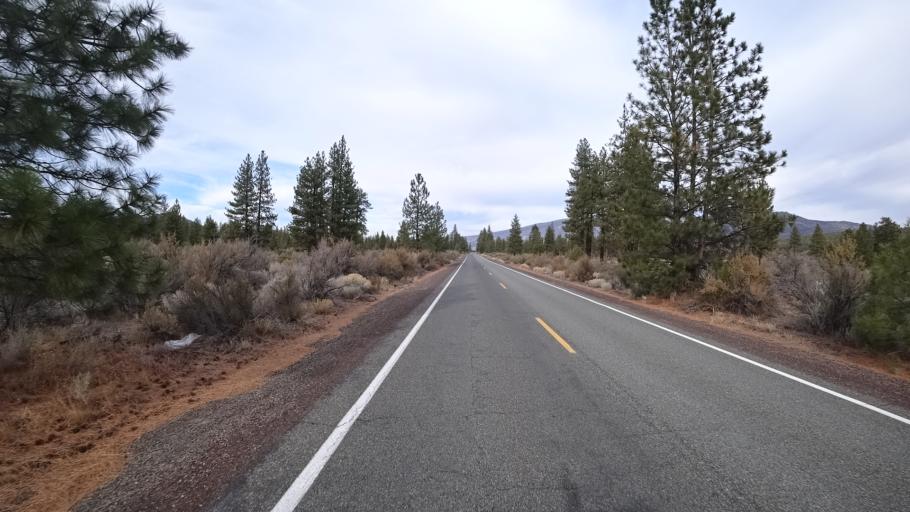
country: US
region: California
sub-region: Siskiyou County
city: Weed
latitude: 41.5408
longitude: -122.2454
